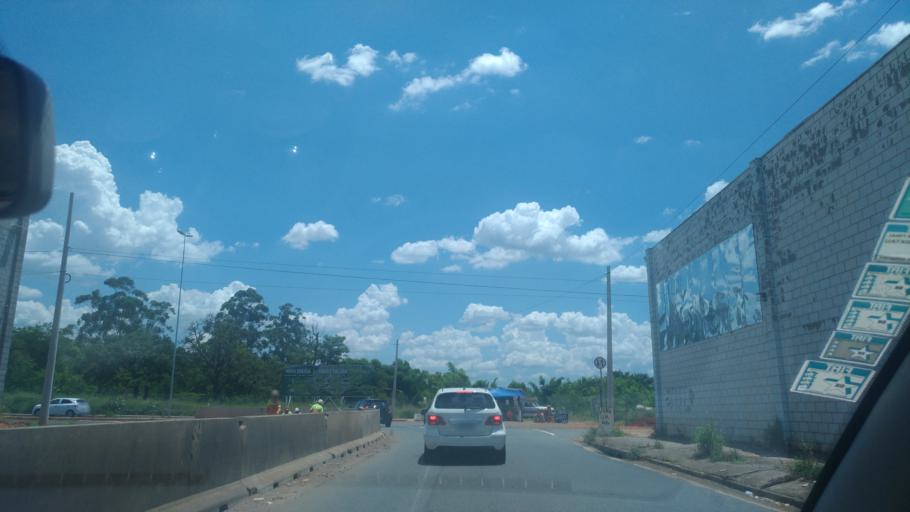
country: BR
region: Sao Paulo
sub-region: Nova Odessa
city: Nova Odessa
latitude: -22.7644
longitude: -47.3192
